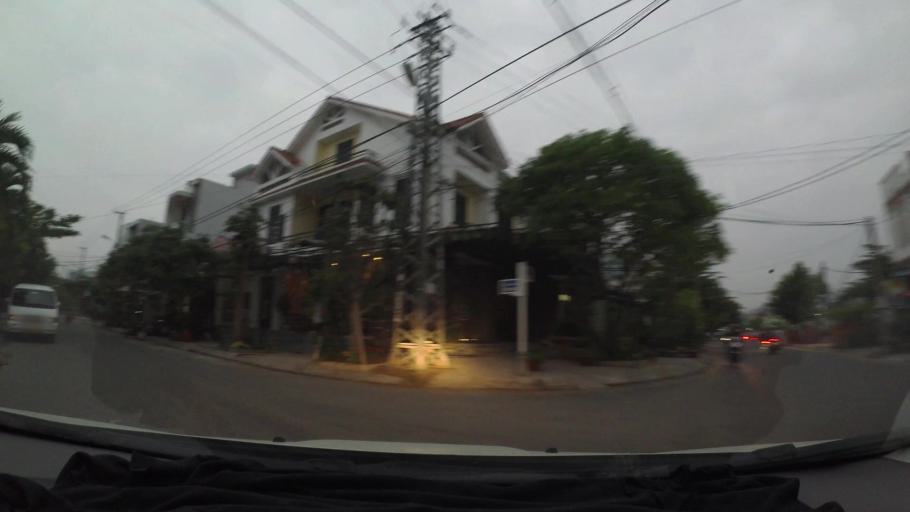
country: VN
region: Da Nang
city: Lien Chieu
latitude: 16.0503
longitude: 108.1704
